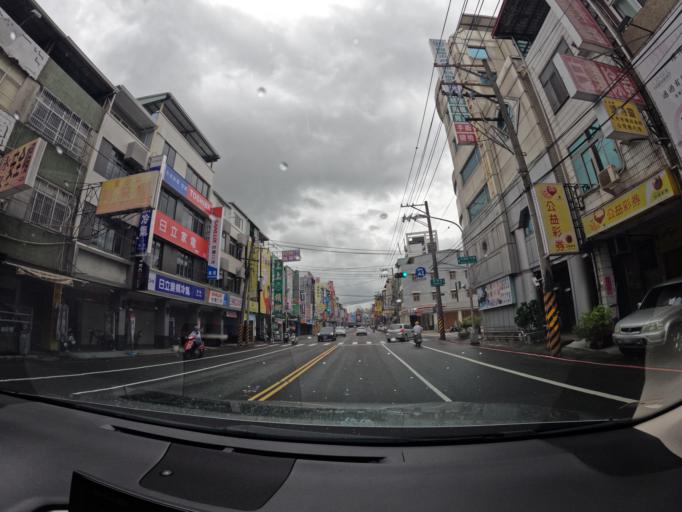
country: TW
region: Taiwan
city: Fengshan
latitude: 22.6240
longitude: 120.3659
